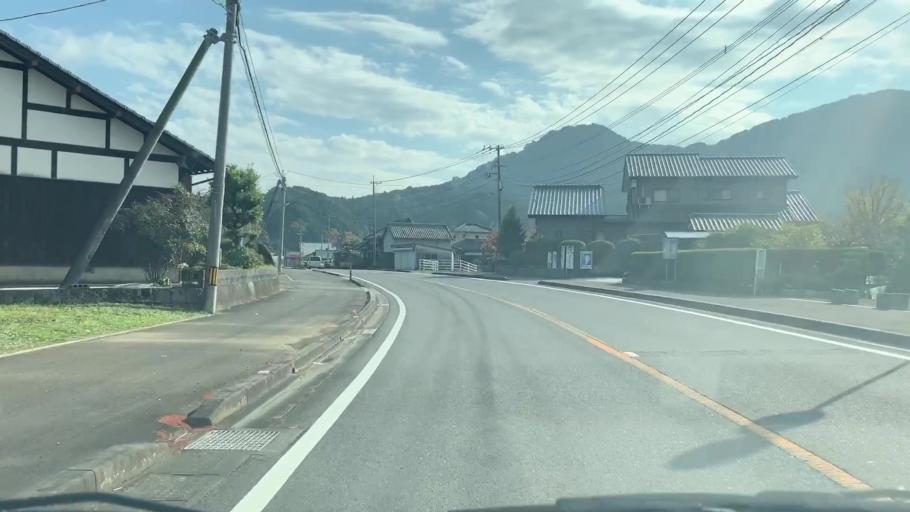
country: JP
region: Saga Prefecture
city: Takeocho-takeo
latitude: 33.1714
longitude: 130.0497
